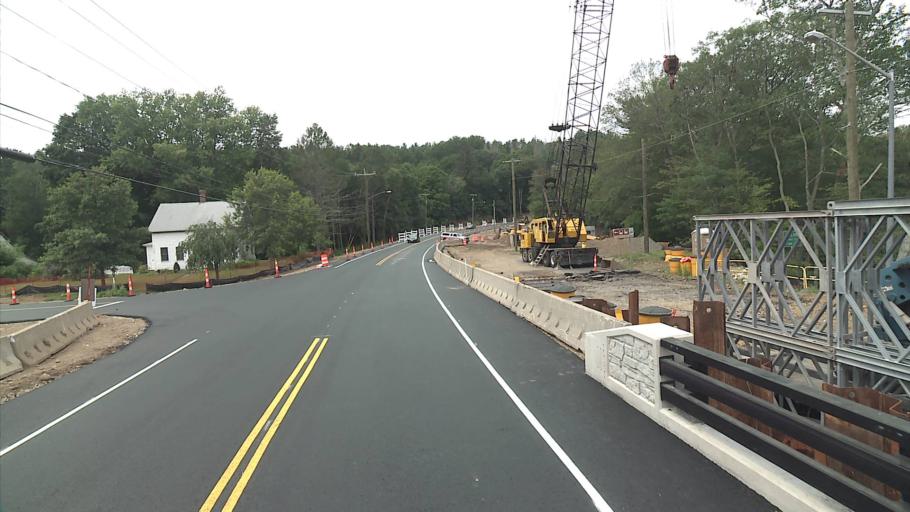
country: US
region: Connecticut
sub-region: Tolland County
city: Tolland
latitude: 41.8814
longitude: -72.3068
